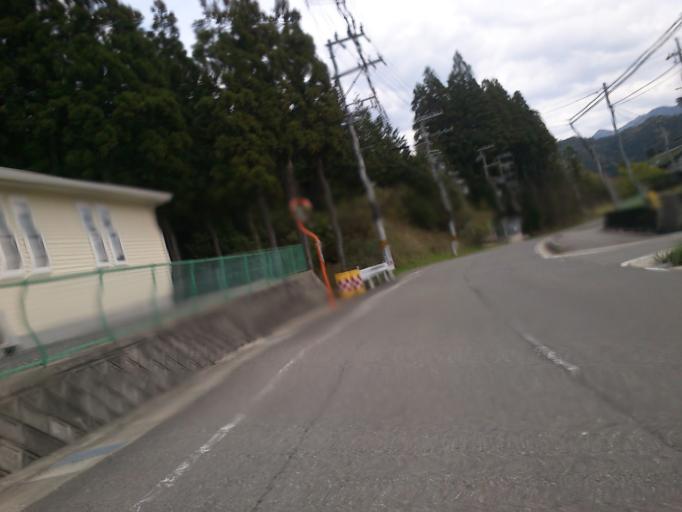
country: JP
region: Kyoto
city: Kameoka
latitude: 35.1979
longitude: 135.6328
